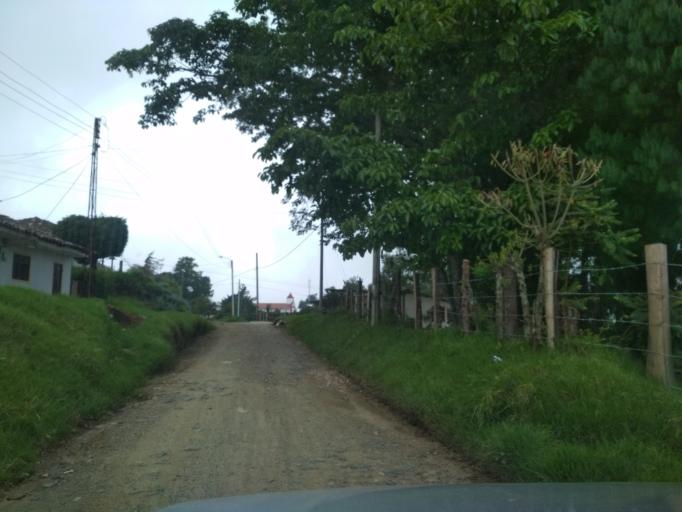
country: CO
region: Cauca
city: Paispamba
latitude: 2.2561
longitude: -76.6133
